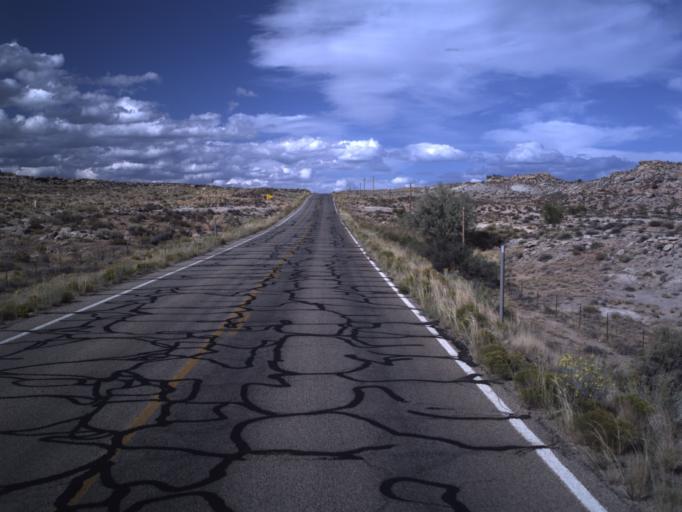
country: US
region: Utah
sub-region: San Juan County
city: Blanding
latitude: 37.2708
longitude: -109.3005
